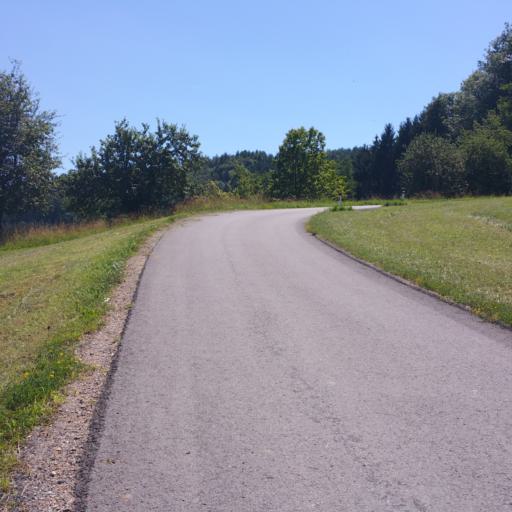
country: AT
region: Styria
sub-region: Politischer Bezirk Leibnitz
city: Gleinstatten
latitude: 46.7381
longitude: 15.3512
